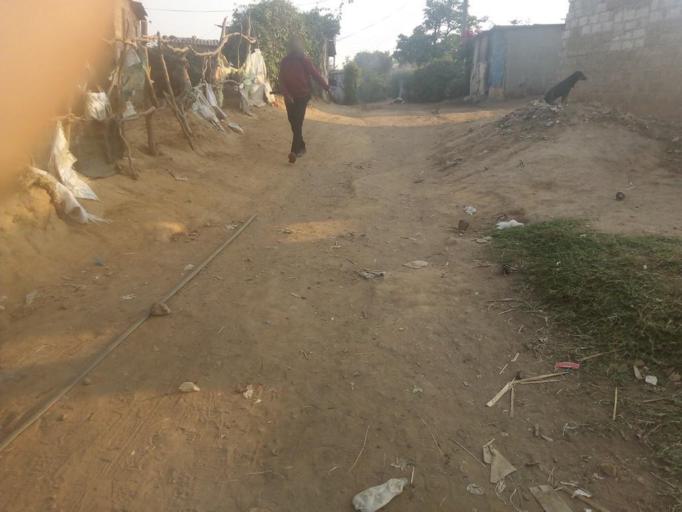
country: ZM
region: Lusaka
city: Lusaka
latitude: -15.4084
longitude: 28.3635
